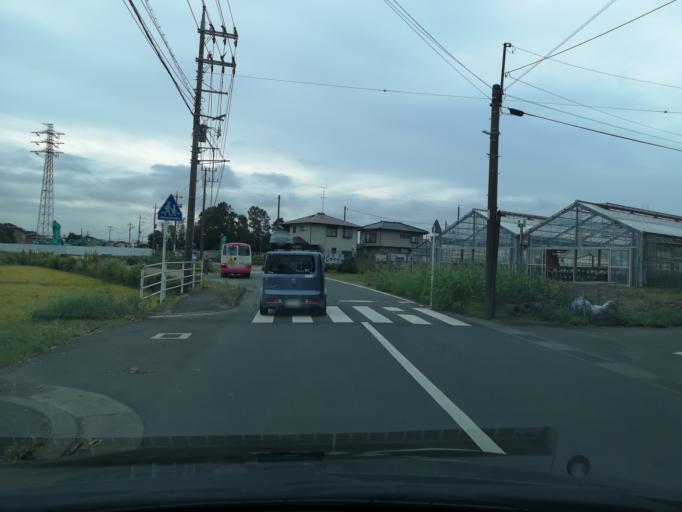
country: JP
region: Kanagawa
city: Atsugi
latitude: 35.3874
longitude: 139.3927
